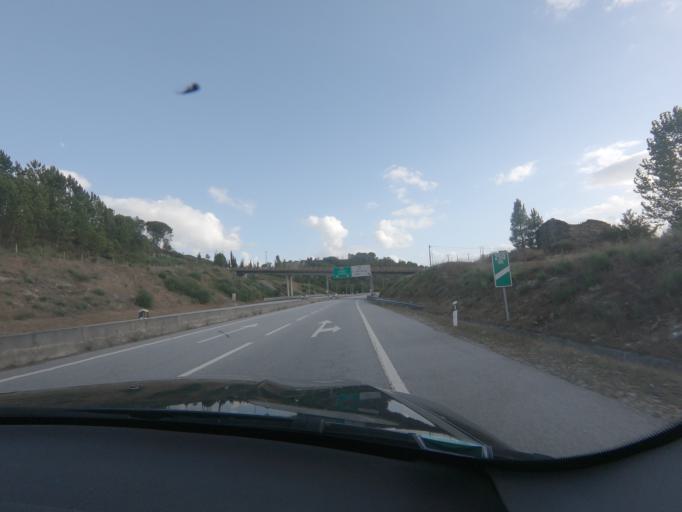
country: PT
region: Viseu
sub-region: Viseu
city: Viseu
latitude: 40.6165
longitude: -7.9634
